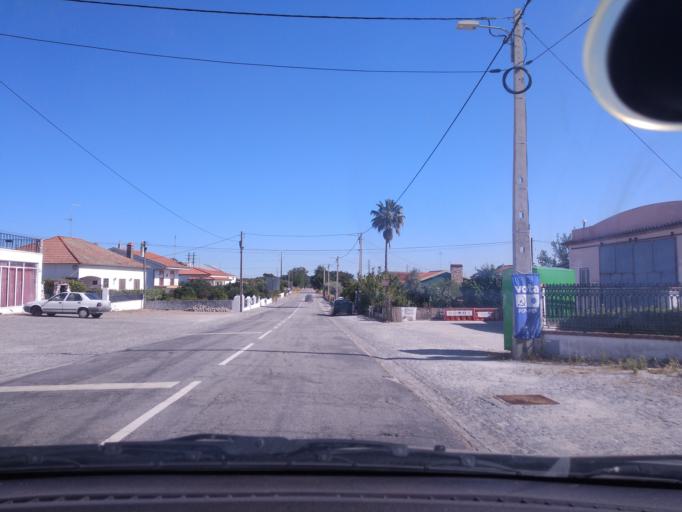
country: PT
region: Portalegre
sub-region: Nisa
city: Nisa
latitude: 39.4217
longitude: -7.6197
